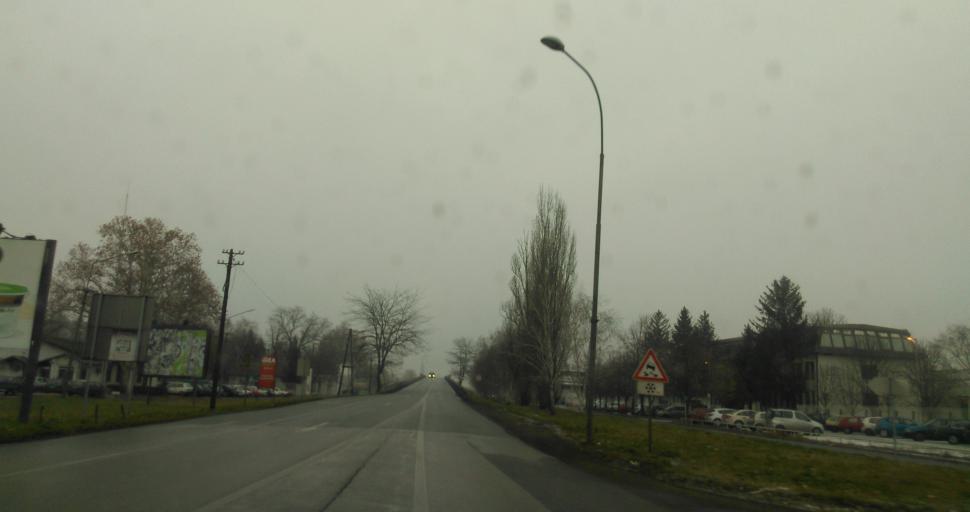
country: RS
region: Autonomna Pokrajina Vojvodina
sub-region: Srednjebanatski Okrug
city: Zrenjanin
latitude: 45.3727
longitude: 20.4154
